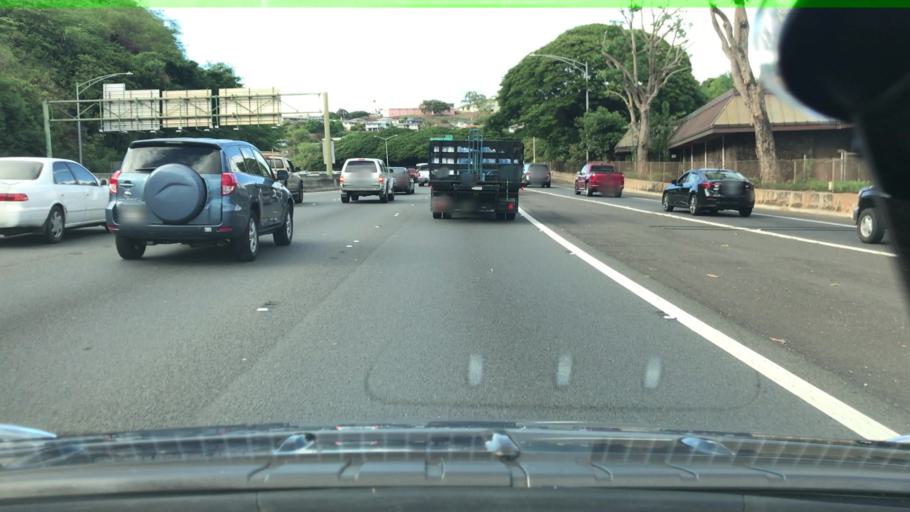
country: US
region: Hawaii
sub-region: Honolulu County
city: Halawa Heights
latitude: 21.3515
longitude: -157.8963
